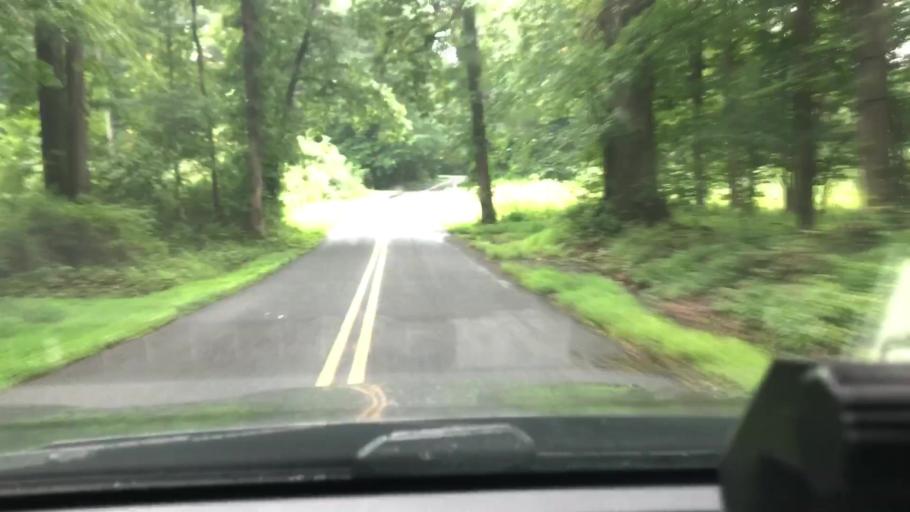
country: US
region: Pennsylvania
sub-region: Lehigh County
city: Macungie
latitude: 40.4758
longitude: -75.5476
